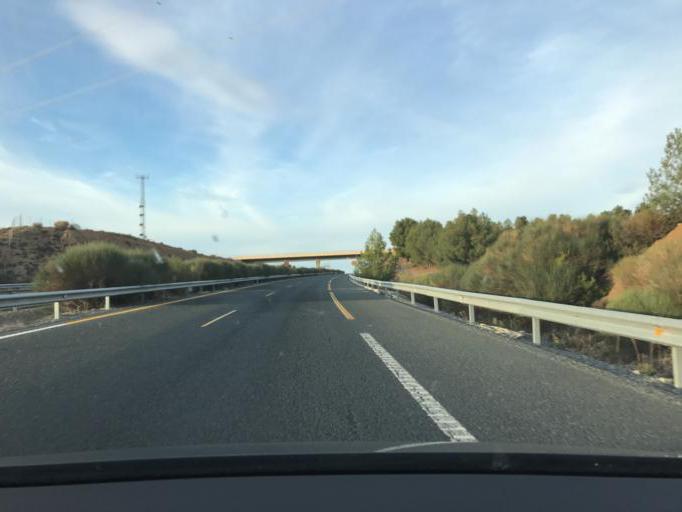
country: ES
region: Andalusia
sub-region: Provincia de Granada
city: Guadix
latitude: 37.2699
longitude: -3.0950
